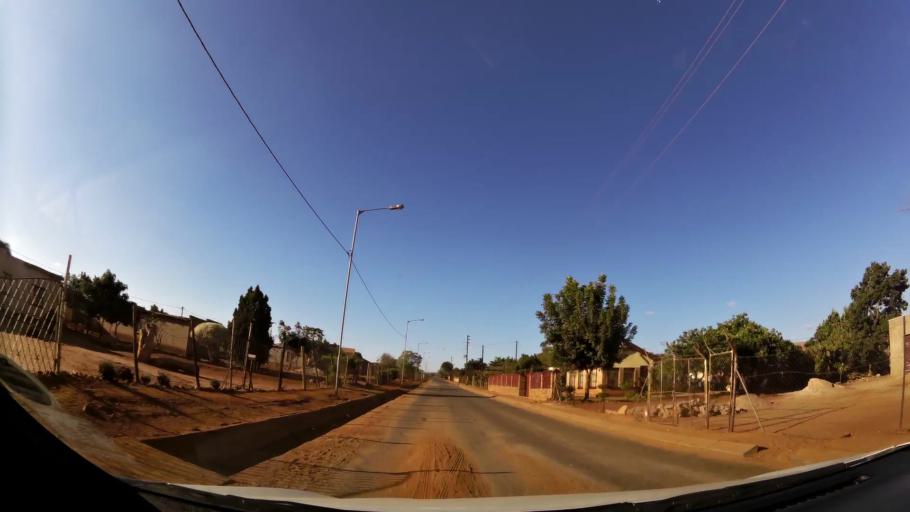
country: ZA
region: Limpopo
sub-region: Waterberg District Municipality
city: Mokopane
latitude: -24.1618
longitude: 28.9850
